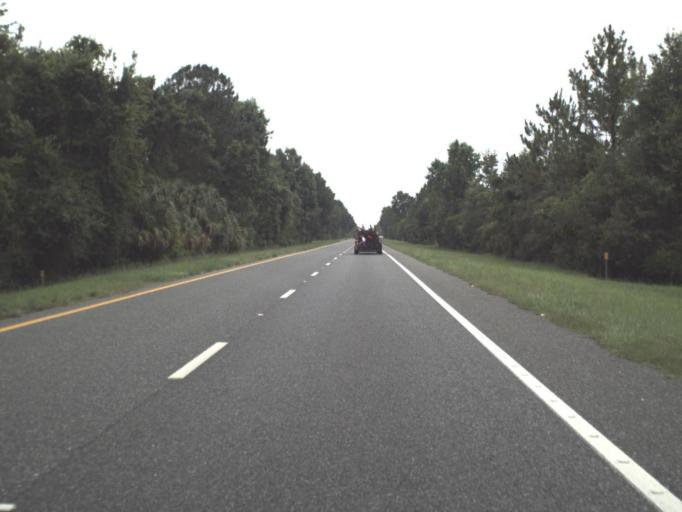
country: US
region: Florida
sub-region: Levy County
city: Bronson
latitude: 29.2954
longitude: -82.7489
